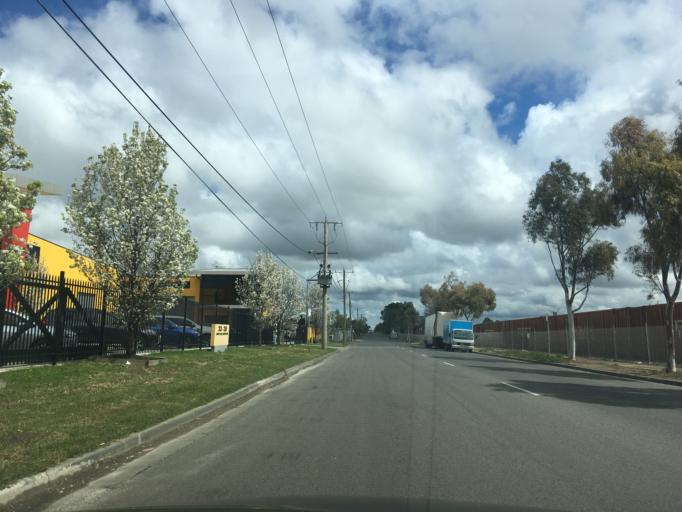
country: AU
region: Victoria
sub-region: Brimbank
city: Brooklyn
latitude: -37.8330
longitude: 144.8055
